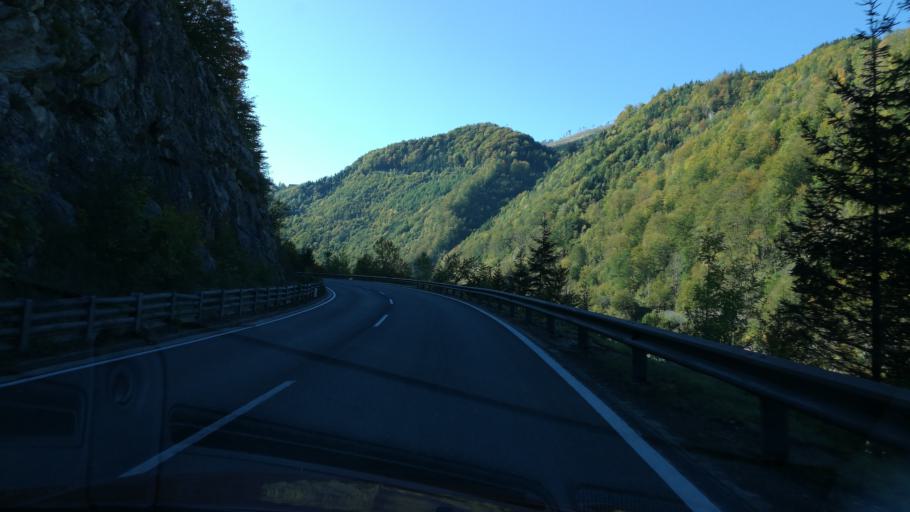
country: AT
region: Upper Austria
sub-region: Politischer Bezirk Steyr-Land
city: Weyer
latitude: 47.8498
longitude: 14.6400
